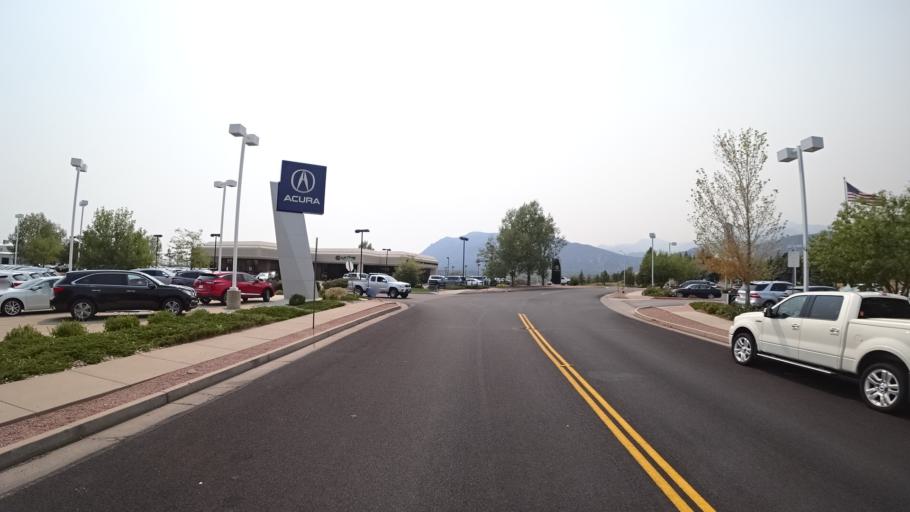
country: US
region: Colorado
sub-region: El Paso County
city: Colorado Springs
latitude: 38.8164
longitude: -104.8405
